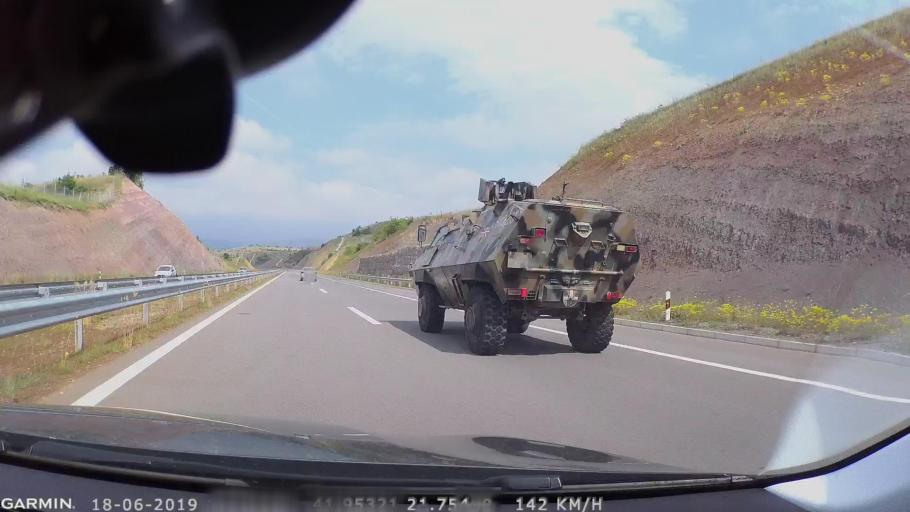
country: MK
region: Sveti Nikole
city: Gorobinci
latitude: 41.9252
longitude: 21.8380
